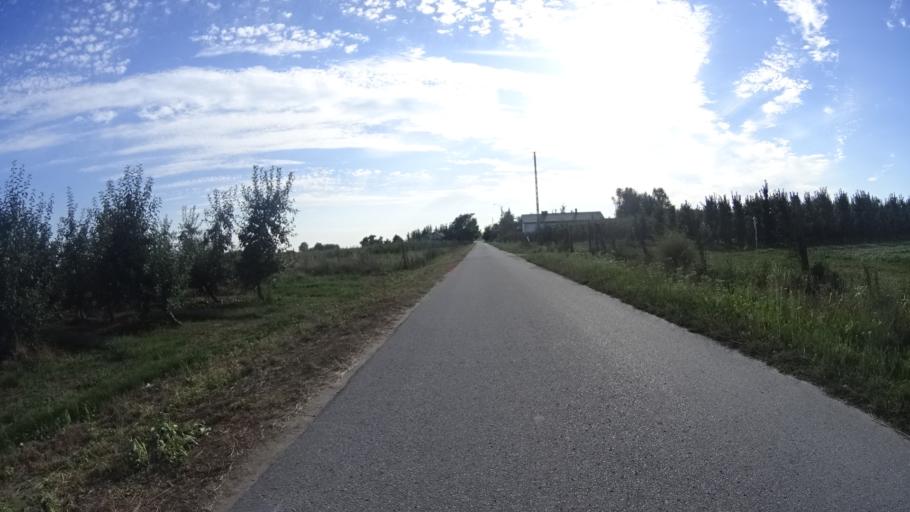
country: PL
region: Masovian Voivodeship
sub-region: Powiat grojecki
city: Goszczyn
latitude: 51.6839
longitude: 20.8335
